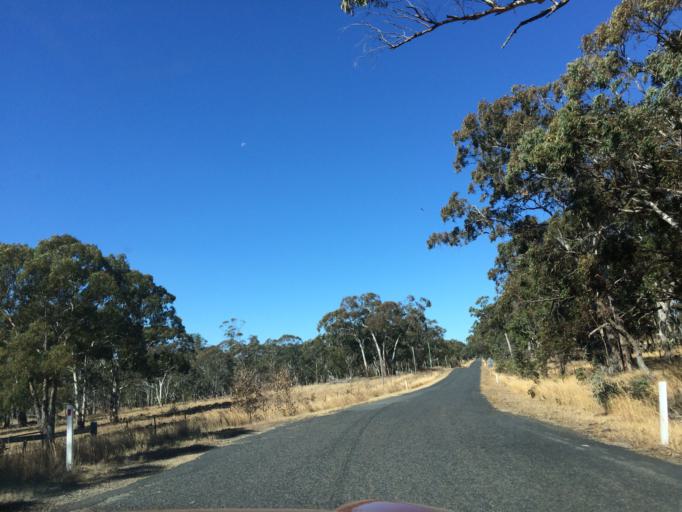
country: AU
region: Queensland
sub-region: Southern Downs
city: Stanthorpe
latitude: -28.6902
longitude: 152.0267
